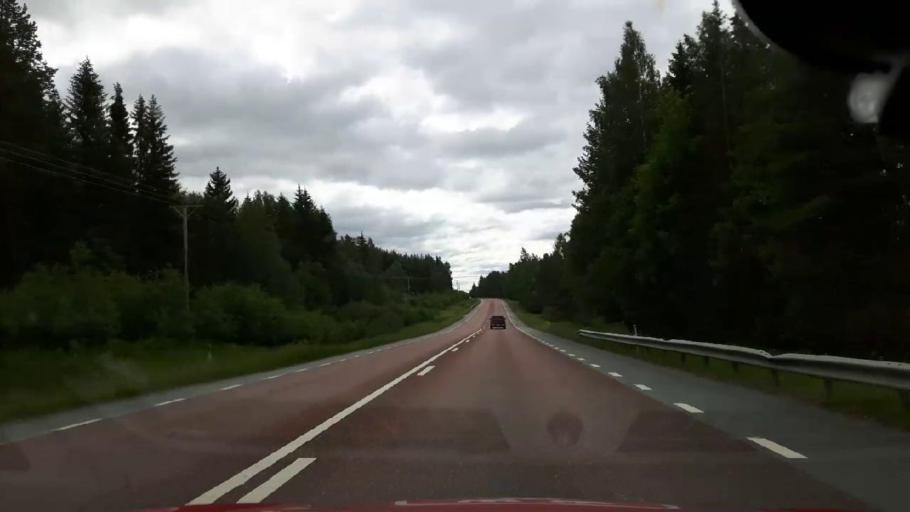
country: SE
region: Jaemtland
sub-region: Braecke Kommun
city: Braecke
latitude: 62.7966
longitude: 15.3733
